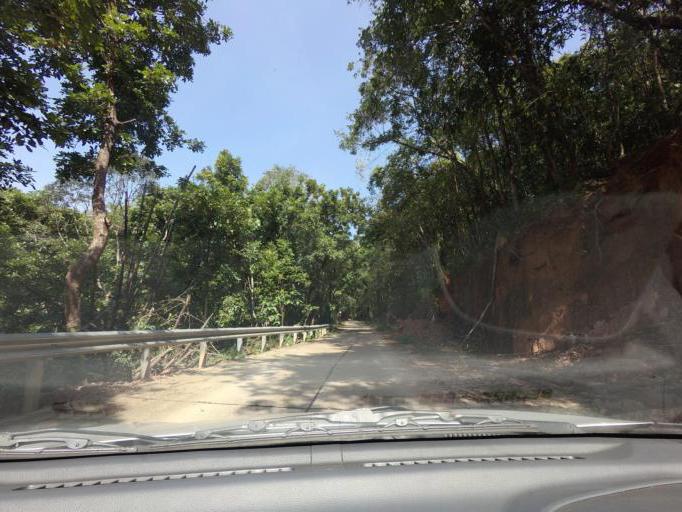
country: IN
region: Karnataka
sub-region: Kodagu
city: Somvarpet
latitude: 12.6957
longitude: 75.6338
